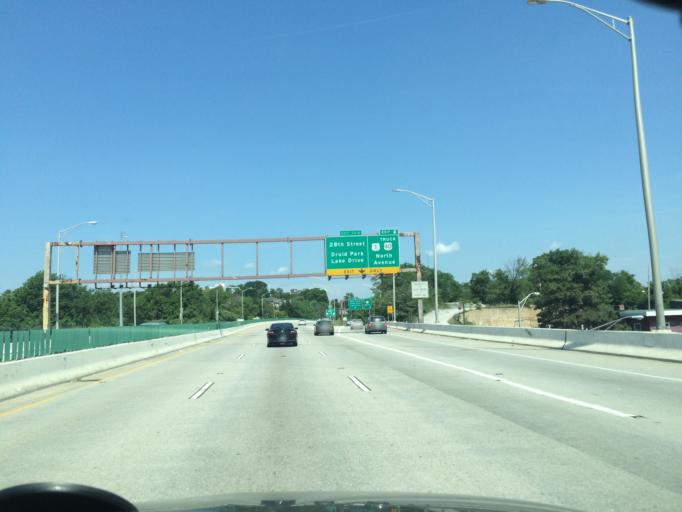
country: US
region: Maryland
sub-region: City of Baltimore
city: Baltimore
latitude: 39.3109
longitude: -76.6230
